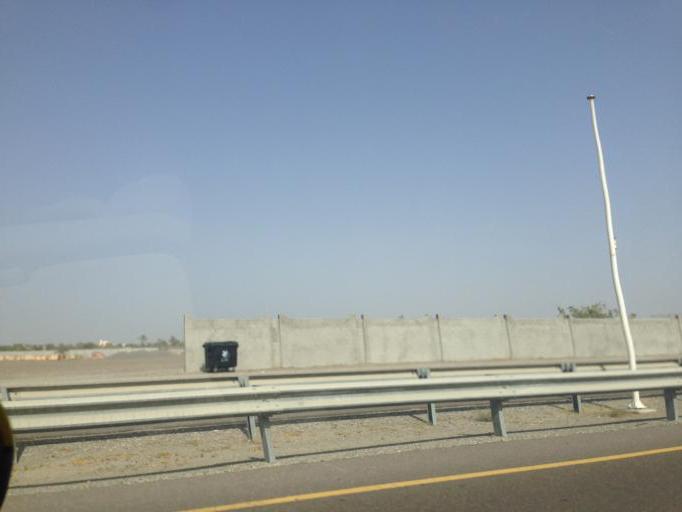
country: OM
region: Al Batinah
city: Barka'
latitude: 23.6719
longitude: 58.0278
